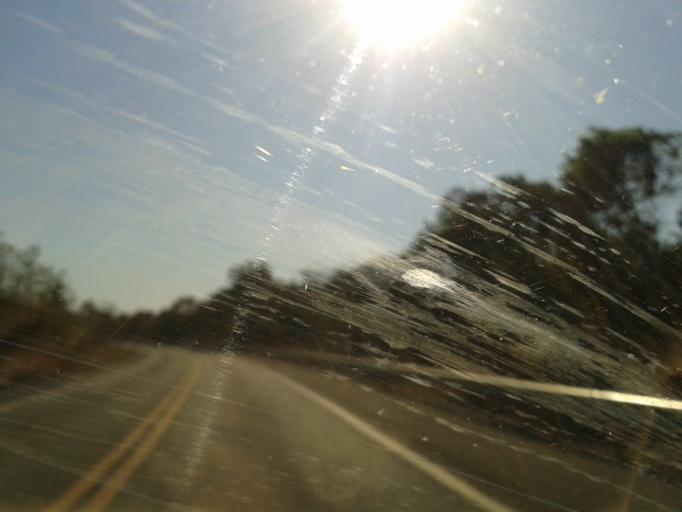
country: BR
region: Goias
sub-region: Mozarlandia
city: Mozarlandia
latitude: -14.9283
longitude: -50.5553
